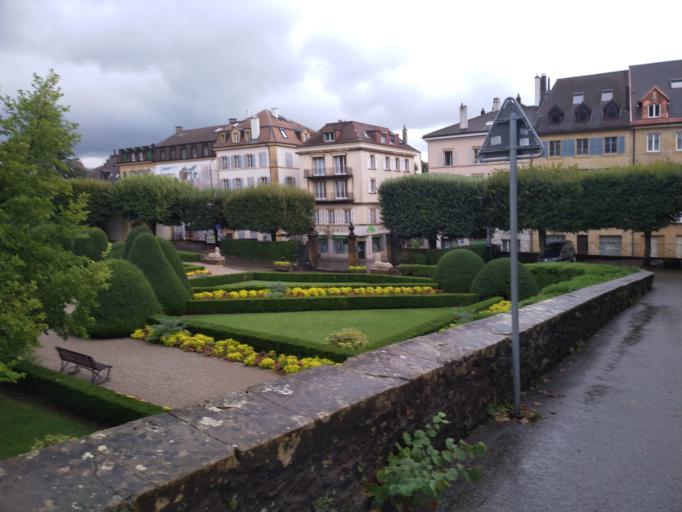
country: CH
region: Neuchatel
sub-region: Neuchatel District
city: Neuchatel
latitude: 46.9937
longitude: 6.9333
